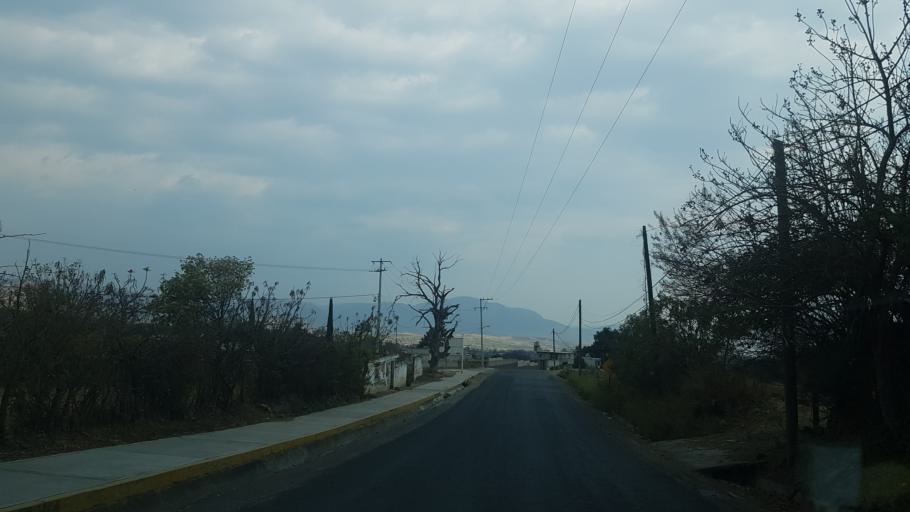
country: MX
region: Puebla
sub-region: Santa Isabel Cholula
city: San Martin Tlamapa
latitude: 18.9759
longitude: -98.3955
